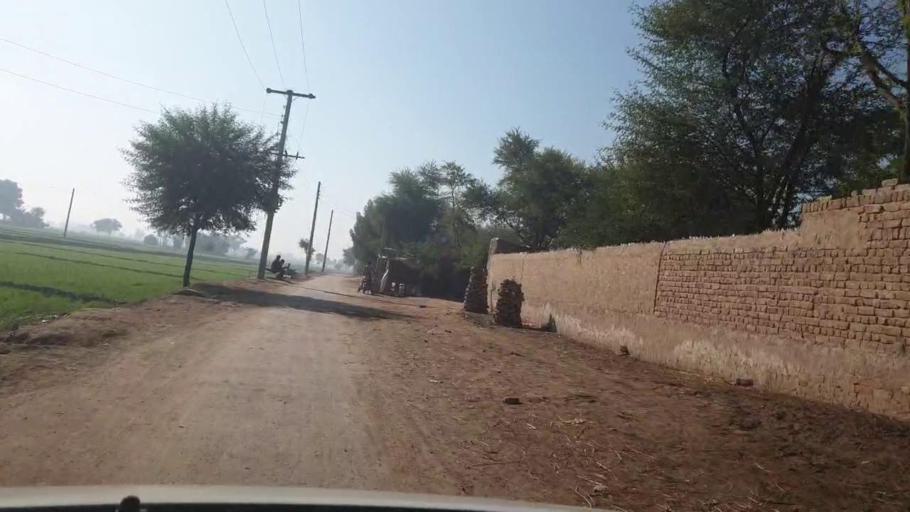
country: PK
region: Sindh
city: Dadu
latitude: 26.6486
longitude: 67.8221
